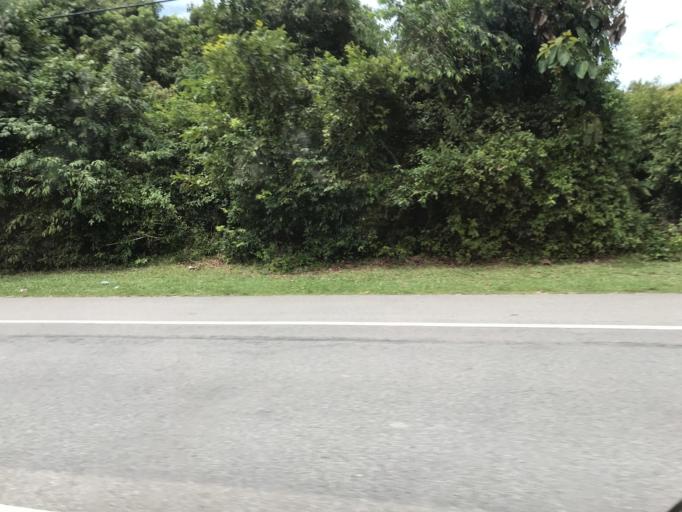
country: MY
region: Kelantan
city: Tumpat
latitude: 6.1727
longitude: 102.2101
